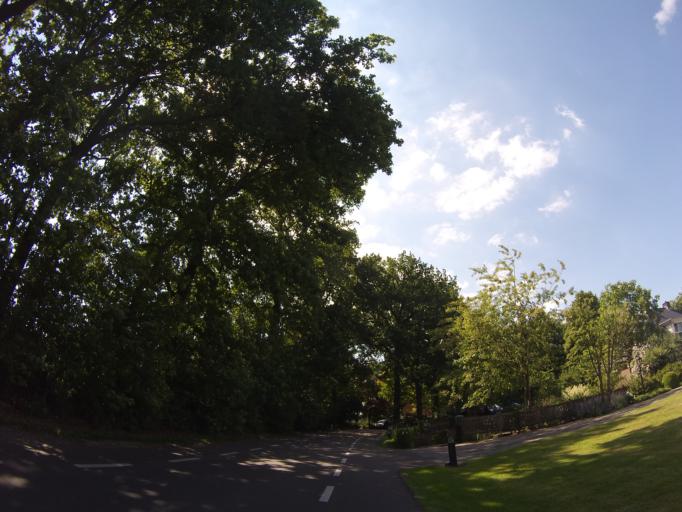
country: NL
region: Gelderland
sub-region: Gemeente Barneveld
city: Barneveld
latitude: 52.1420
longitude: 5.5536
